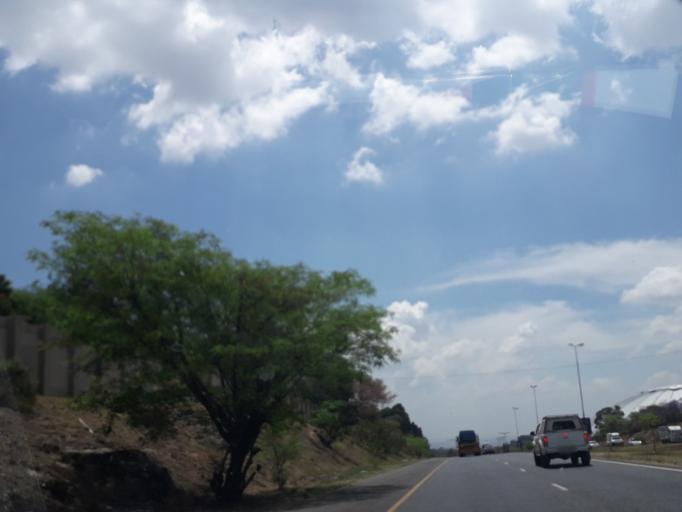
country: ZA
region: Gauteng
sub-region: West Rand District Municipality
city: Muldersdriseloop
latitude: -26.0674
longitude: 27.9391
